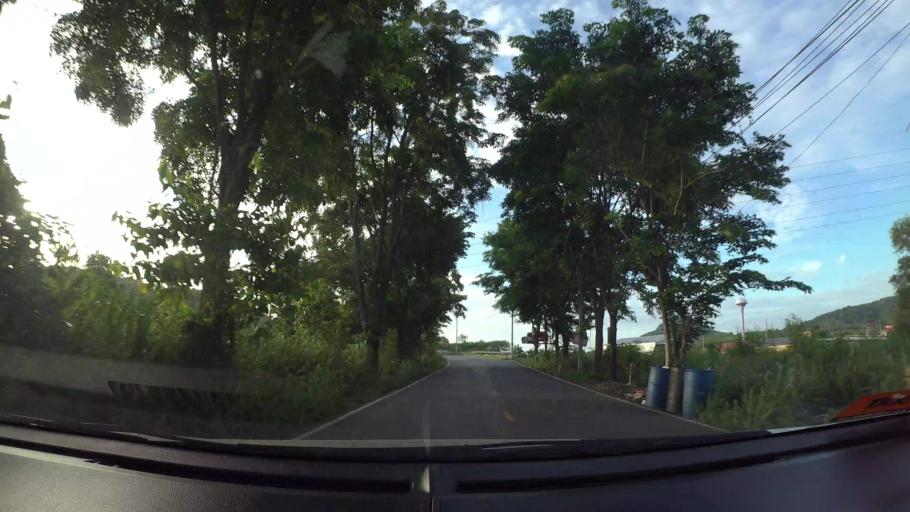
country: TH
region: Chon Buri
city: Sattahip
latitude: 12.7404
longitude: 100.9366
